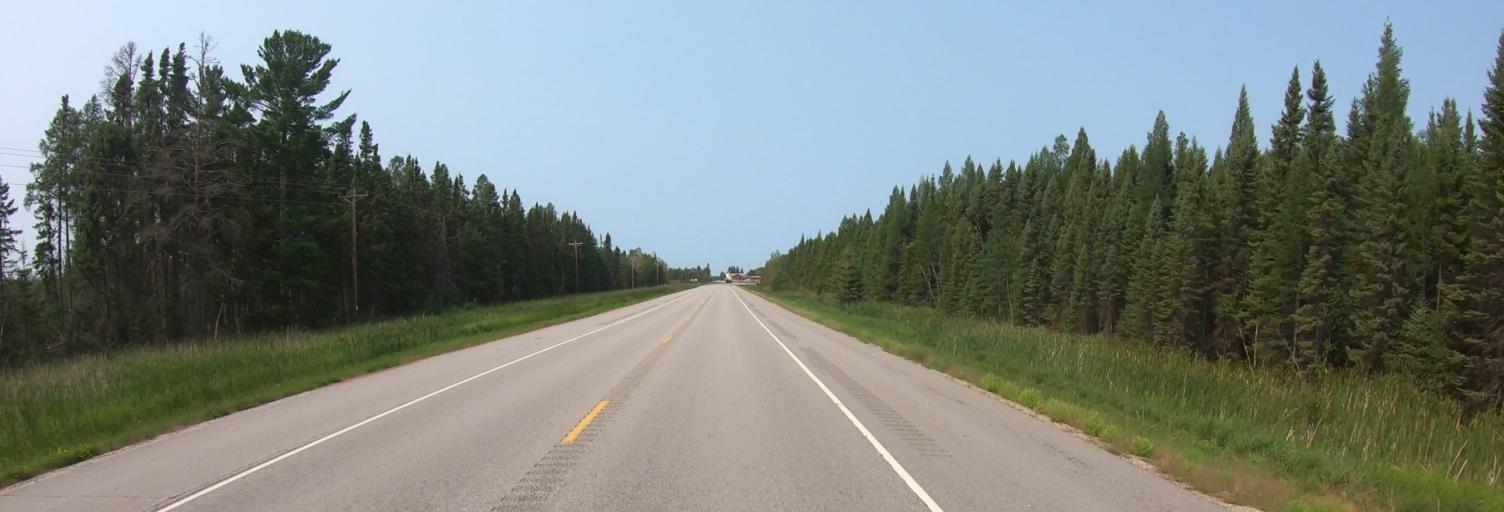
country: CA
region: Ontario
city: Fort Frances
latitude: 48.4107
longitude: -93.1923
